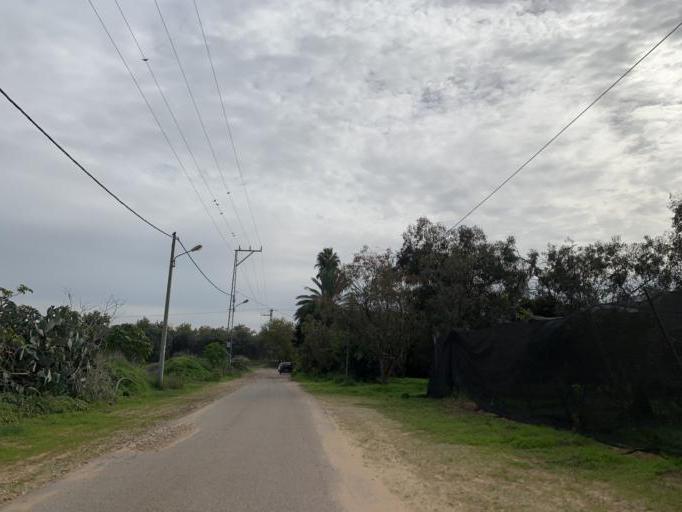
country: IL
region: Central District
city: Hod HaSharon
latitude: 32.1491
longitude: 34.9051
